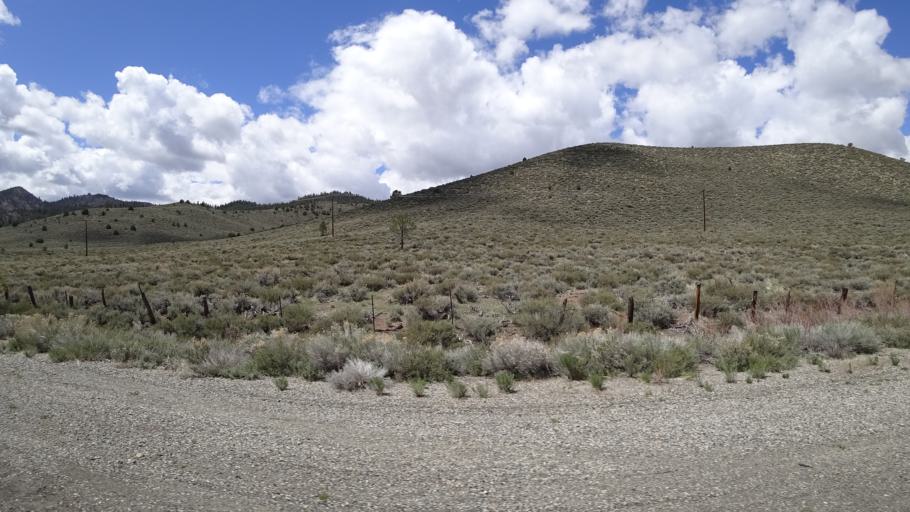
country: US
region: California
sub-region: Mono County
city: Bridgeport
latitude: 38.3050
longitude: -119.3138
